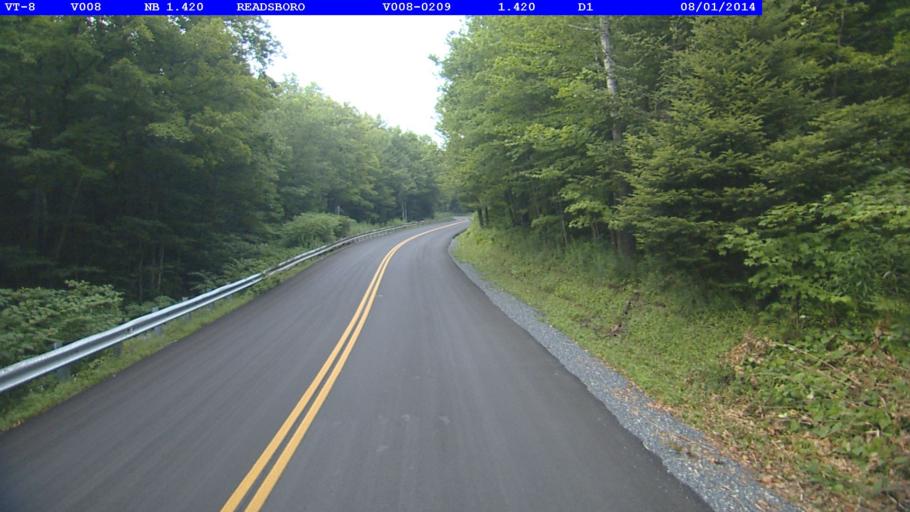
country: US
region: Massachusetts
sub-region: Berkshire County
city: North Adams
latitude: 42.8466
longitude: -72.9893
